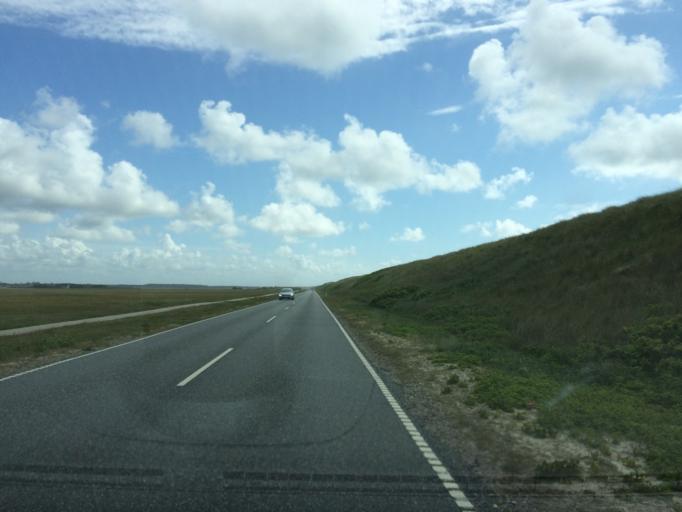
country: DK
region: Central Jutland
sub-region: Holstebro Kommune
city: Ulfborg
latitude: 56.3478
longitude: 8.1225
